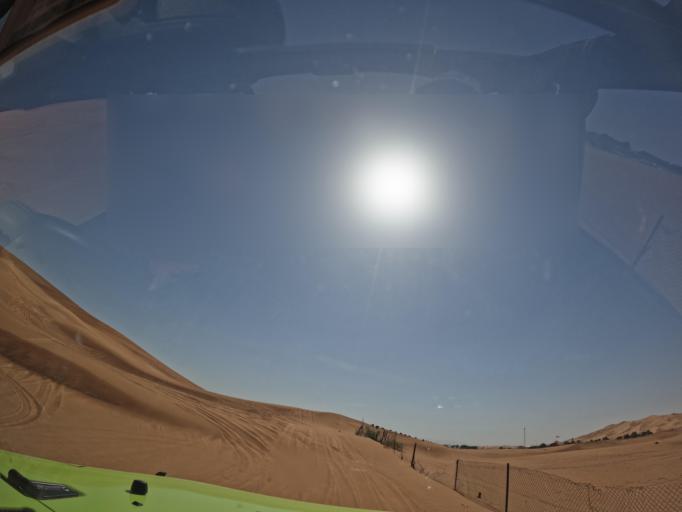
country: AE
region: Ash Shariqah
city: Adh Dhayd
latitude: 24.9581
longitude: 55.7180
